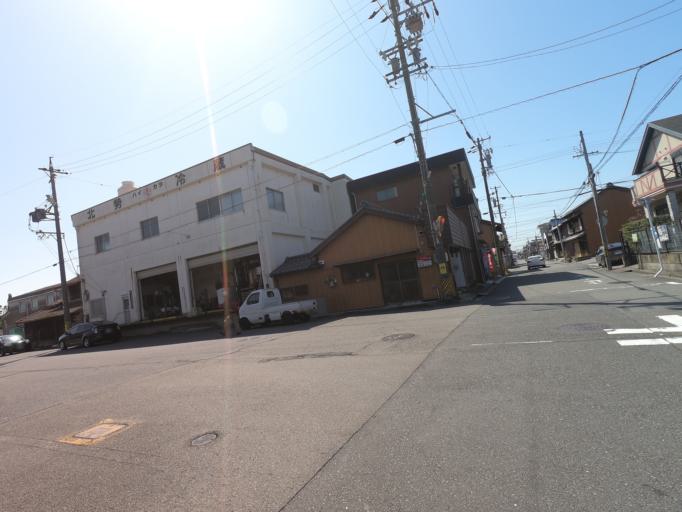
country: JP
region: Mie
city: Yokkaichi
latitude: 35.0065
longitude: 136.6635
